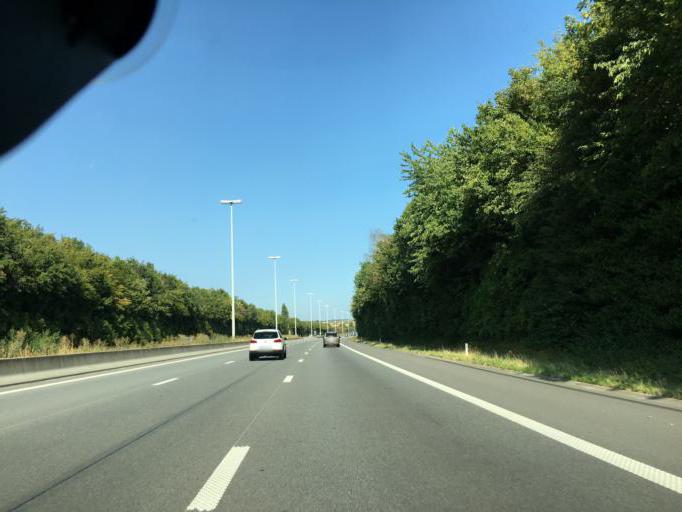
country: BE
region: Wallonia
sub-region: Province de Liege
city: Wanze
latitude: 50.5612
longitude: 5.1622
